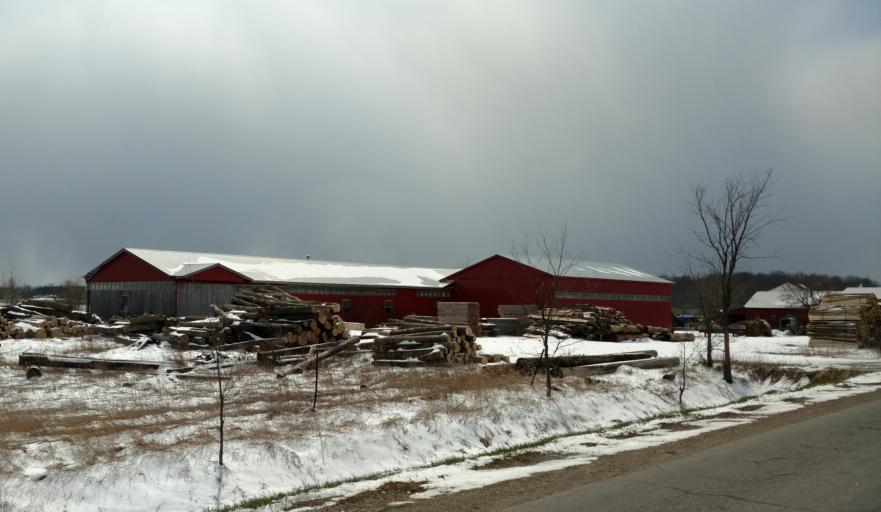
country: US
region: Michigan
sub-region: Gladwin County
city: Gladwin
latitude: 44.0306
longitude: -84.4519
